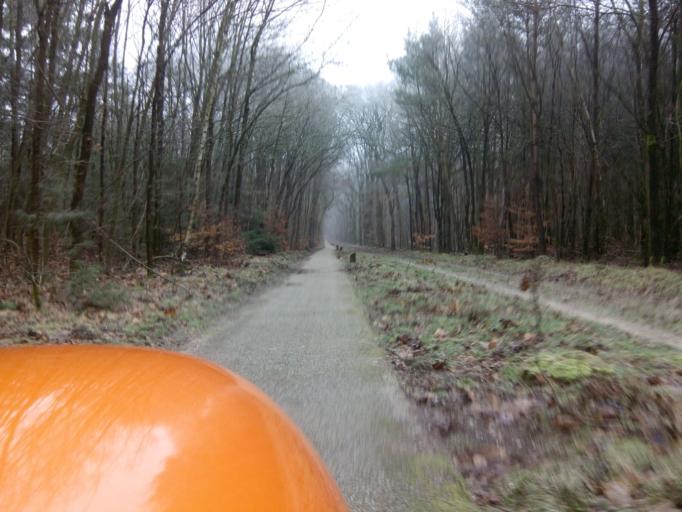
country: NL
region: Gelderland
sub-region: Gemeente Ermelo
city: Ermelo
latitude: 52.2676
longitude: 5.6501
